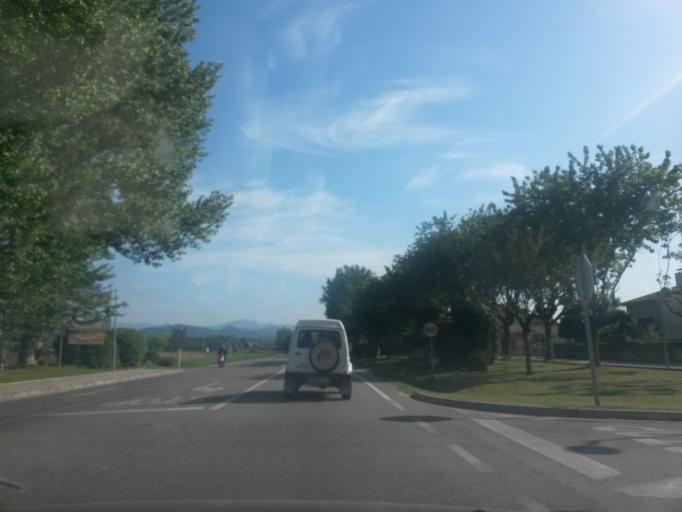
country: ES
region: Catalonia
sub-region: Provincia de Girona
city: Bas
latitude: 42.1484
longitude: 2.4609
